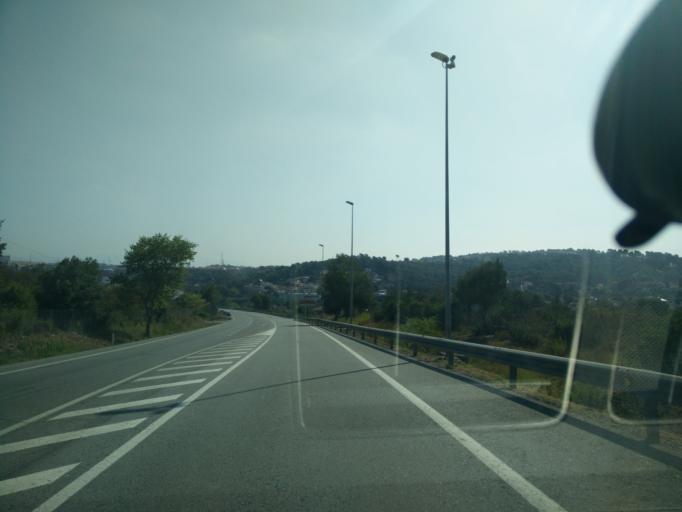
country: ES
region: Catalonia
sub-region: Provincia de Barcelona
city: Rubi
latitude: 41.5301
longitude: 2.0283
